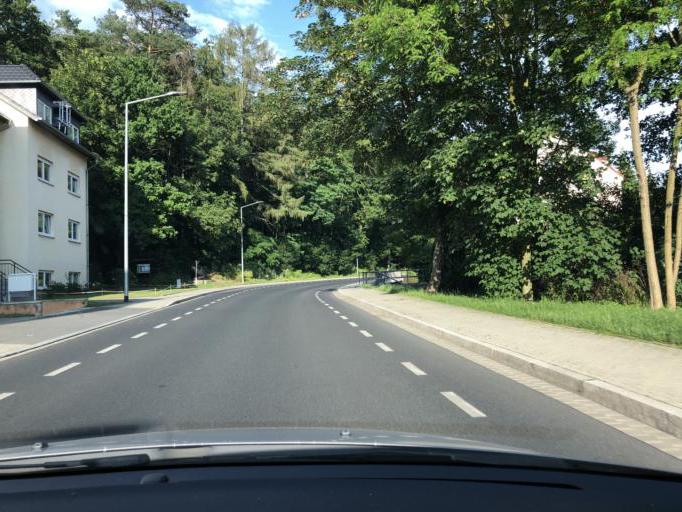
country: DE
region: Saxony
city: Freital
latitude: 50.9862
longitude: 13.6782
